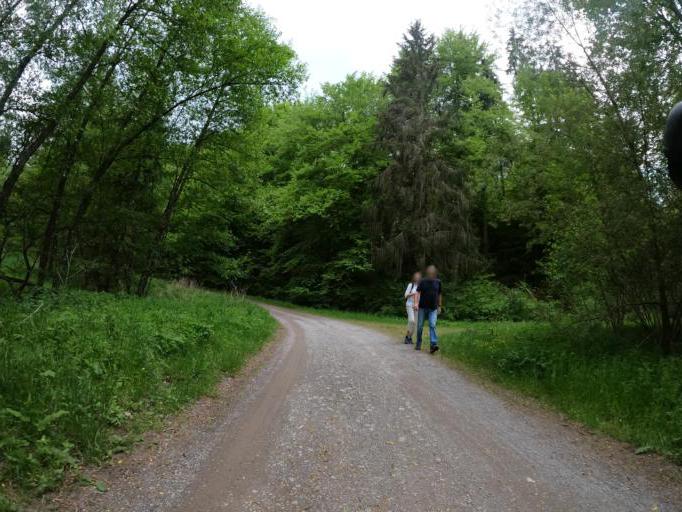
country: DE
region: Baden-Wuerttemberg
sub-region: Tuebingen Region
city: Dettenhausen
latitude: 48.6002
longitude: 9.1198
